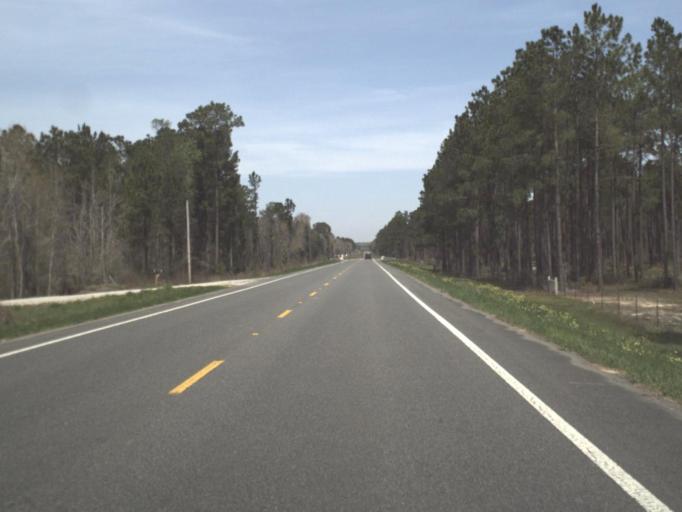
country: US
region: Florida
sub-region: Walton County
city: DeFuniak Springs
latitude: 30.7976
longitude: -85.9585
